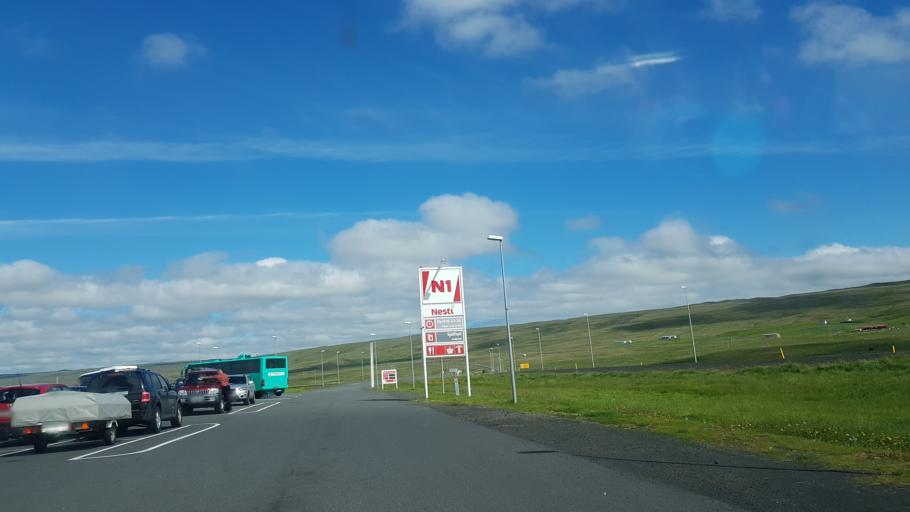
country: IS
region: West
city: Borgarnes
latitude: 65.1441
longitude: -21.0840
